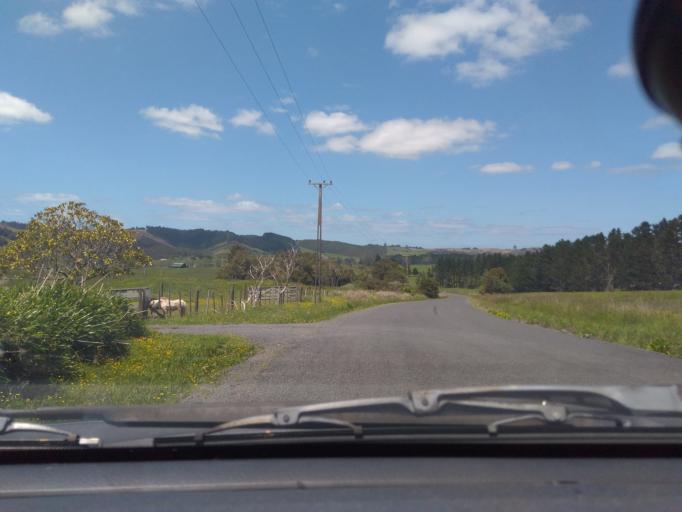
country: NZ
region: Auckland
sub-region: Auckland
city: Pakuranga
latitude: -36.9013
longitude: 175.0110
